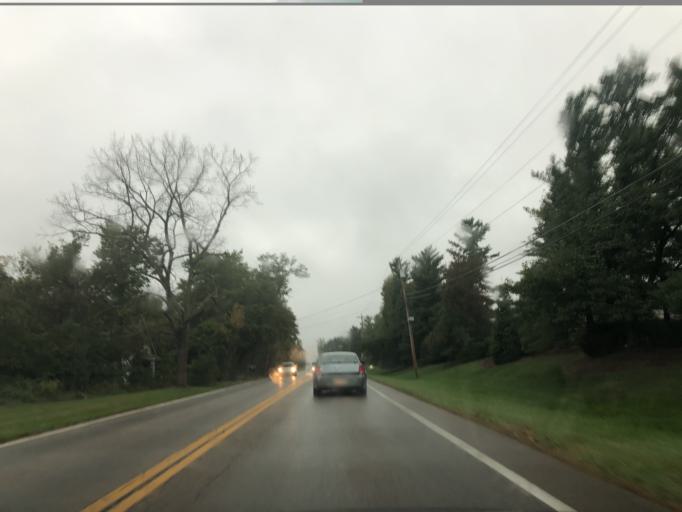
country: US
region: Ohio
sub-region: Clermont County
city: Mulberry
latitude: 39.2223
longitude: -84.2490
